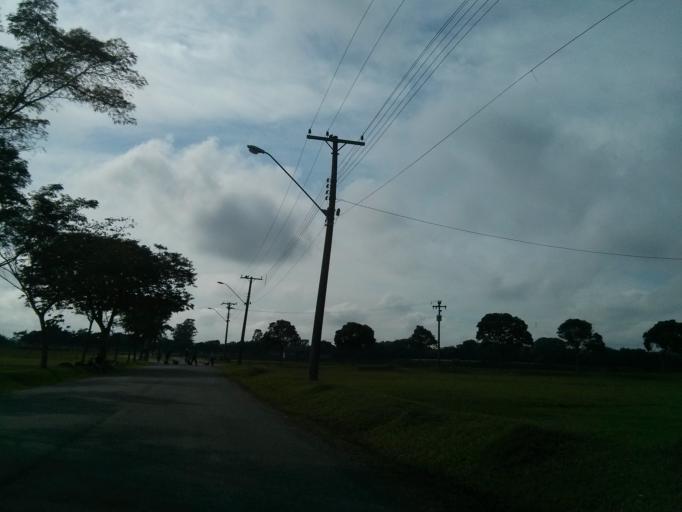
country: BR
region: Parana
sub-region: Sao Jose Dos Pinhais
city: Sao Jose dos Pinhais
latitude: -25.5184
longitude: -49.2204
